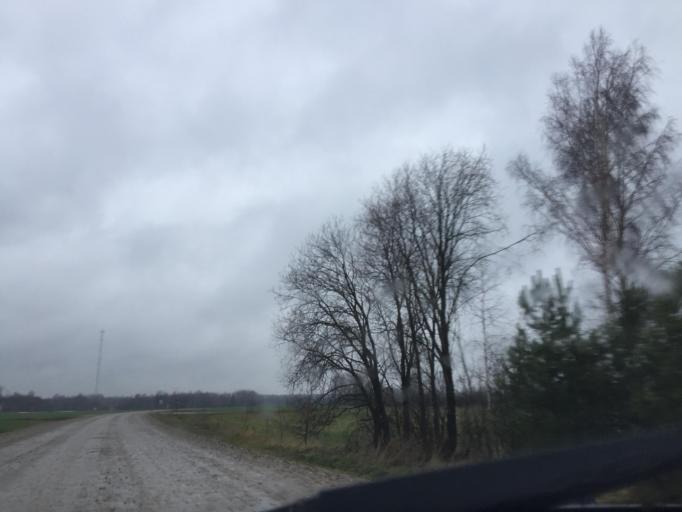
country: LV
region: Salacgrivas
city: Salacgriva
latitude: 57.7657
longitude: 24.5374
